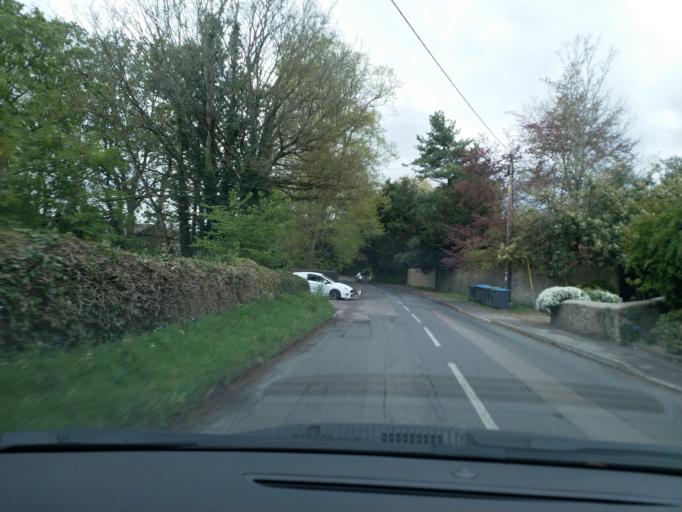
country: GB
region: England
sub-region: Oxfordshire
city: Eynsham
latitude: 51.7963
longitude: -1.3417
